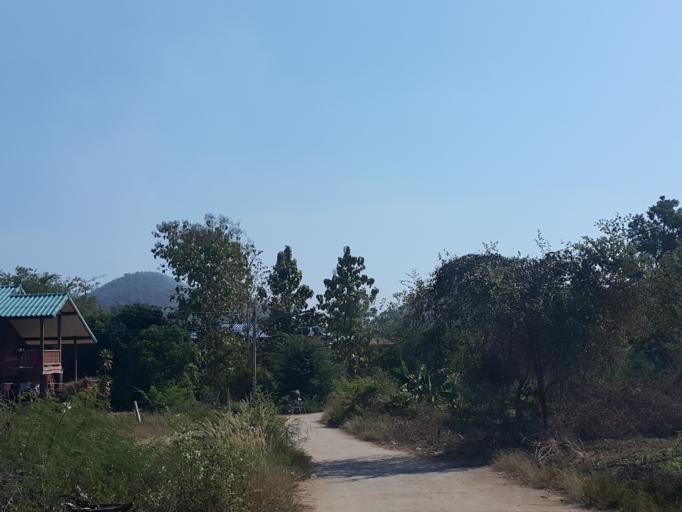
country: TH
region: Sukhothai
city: Thung Saliam
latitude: 17.3436
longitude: 99.4411
